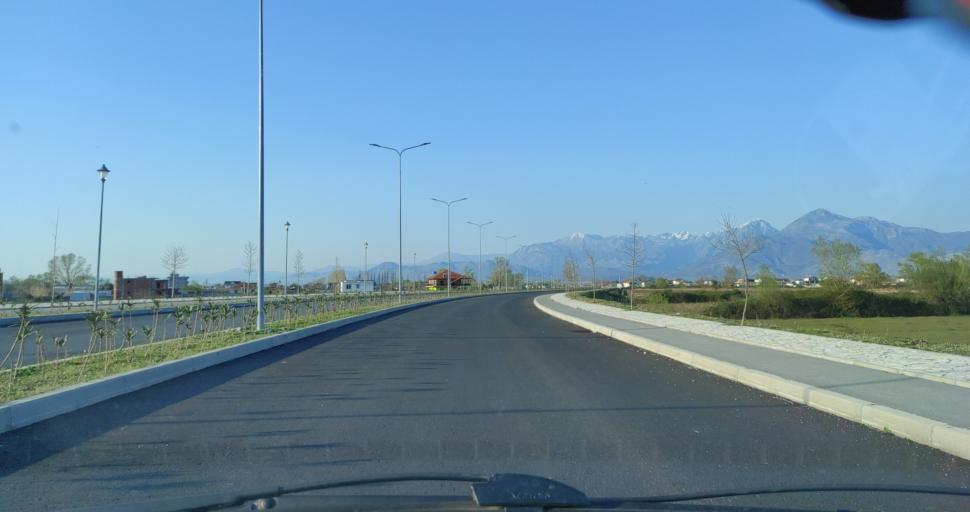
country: AL
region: Shkoder
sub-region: Rrethi i Shkodres
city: Shkoder
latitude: 42.0727
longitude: 19.4896
